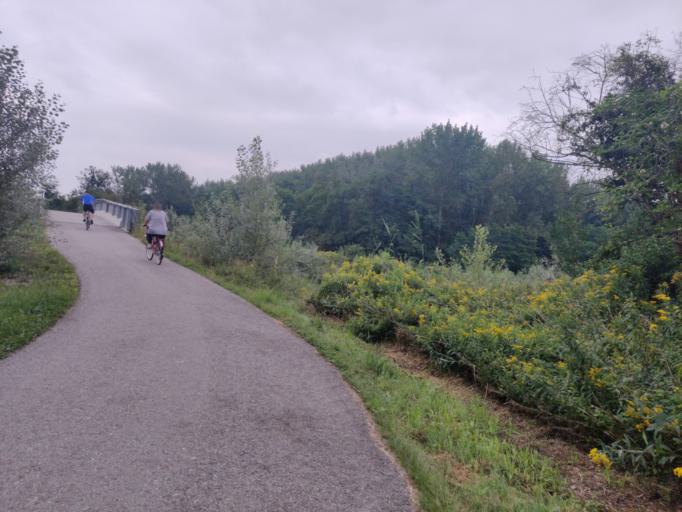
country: AT
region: Lower Austria
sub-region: Politischer Bezirk Tulln
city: Kirchberg am Wagram
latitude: 48.3630
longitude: 15.8718
